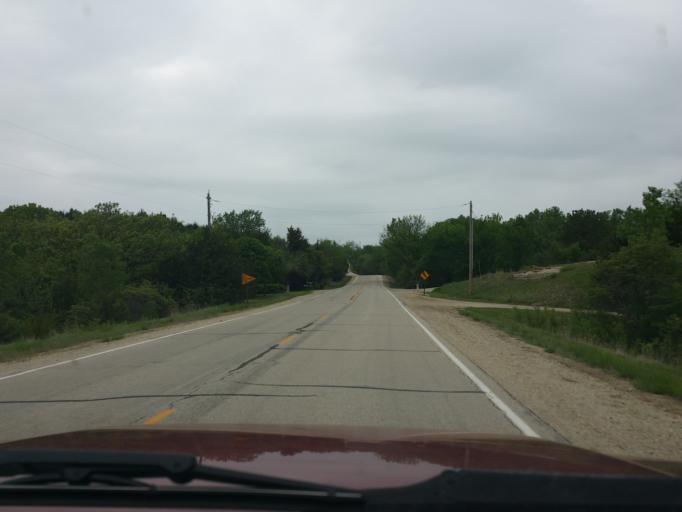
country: US
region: Kansas
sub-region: Riley County
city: Manhattan
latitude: 39.2728
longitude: -96.6280
